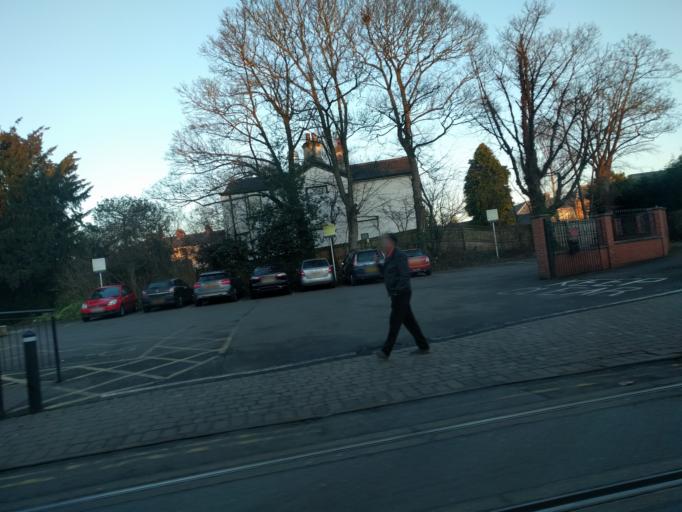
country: GB
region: England
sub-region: Nottingham
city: Nottingham
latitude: 52.9626
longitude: -1.1617
